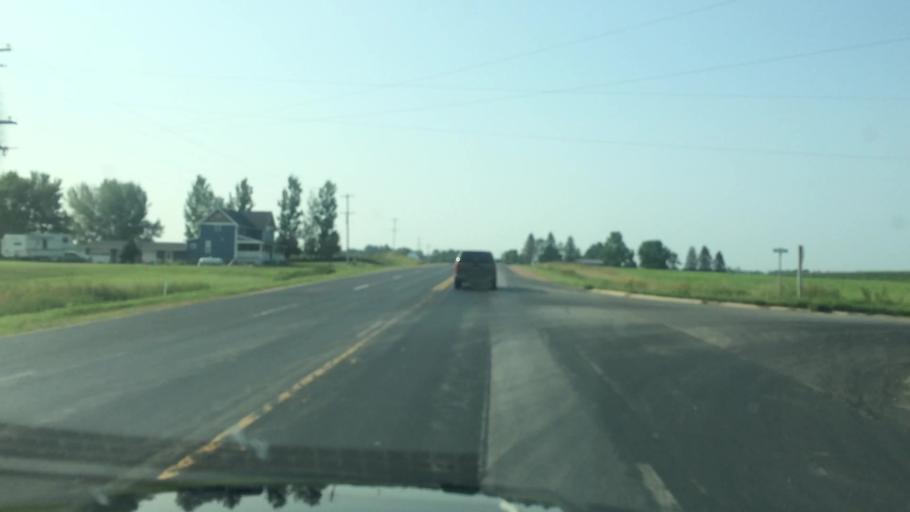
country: US
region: Wisconsin
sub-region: Marathon County
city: Stratford
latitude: 44.8190
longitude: -90.0791
